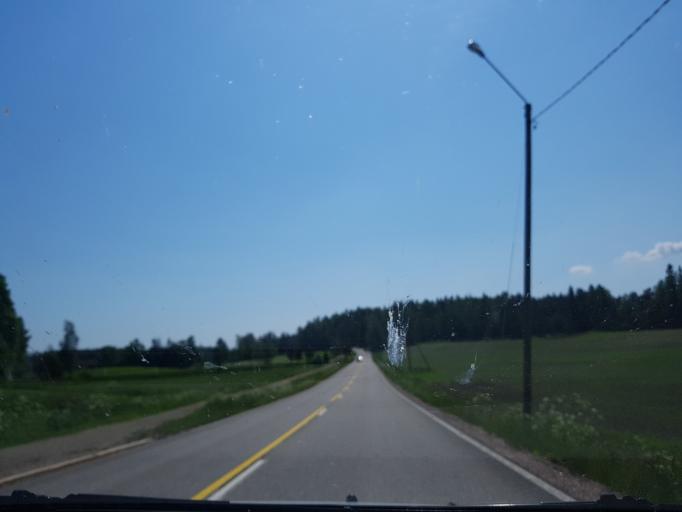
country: FI
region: Uusimaa
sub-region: Helsinki
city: Vihti
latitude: 60.3223
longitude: 24.4043
